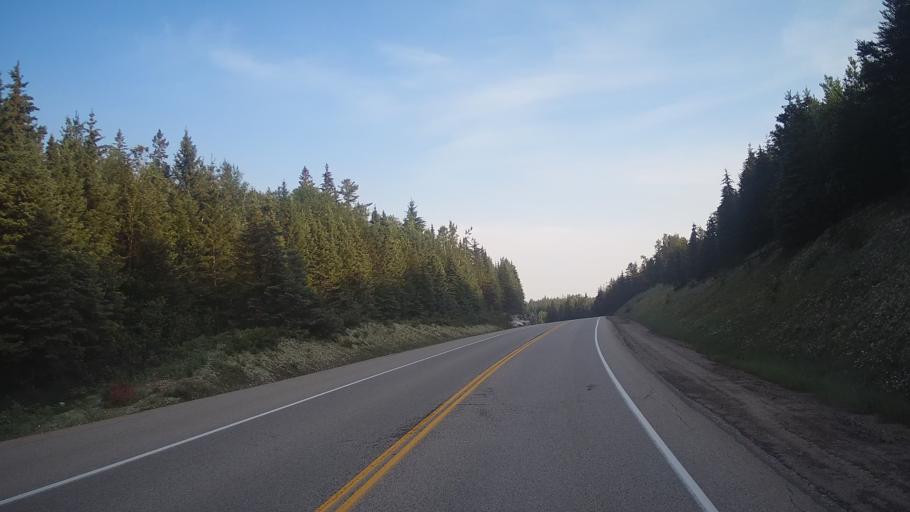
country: CA
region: Ontario
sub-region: Rainy River District
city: Atikokan
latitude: 49.3209
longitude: -91.3996
